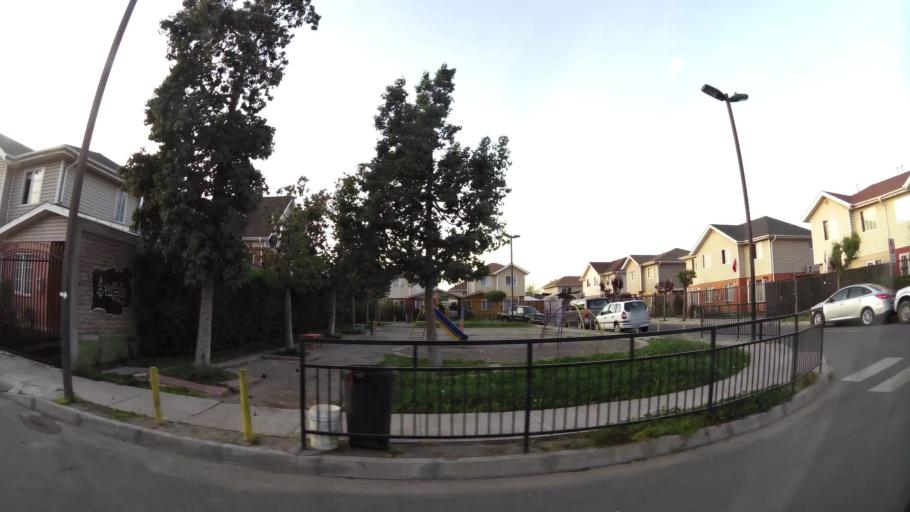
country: CL
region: Santiago Metropolitan
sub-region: Provincia de Cordillera
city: Puente Alto
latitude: -33.5968
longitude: -70.5855
